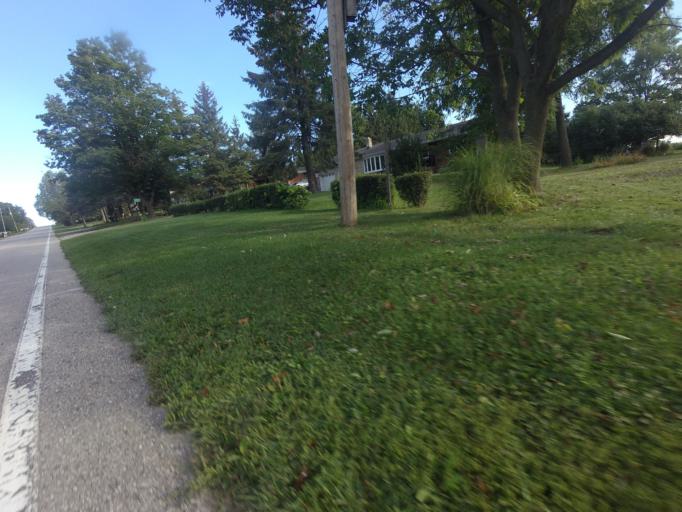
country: CA
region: Ontario
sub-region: Wellington County
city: Guelph
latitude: 43.5988
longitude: -80.3440
